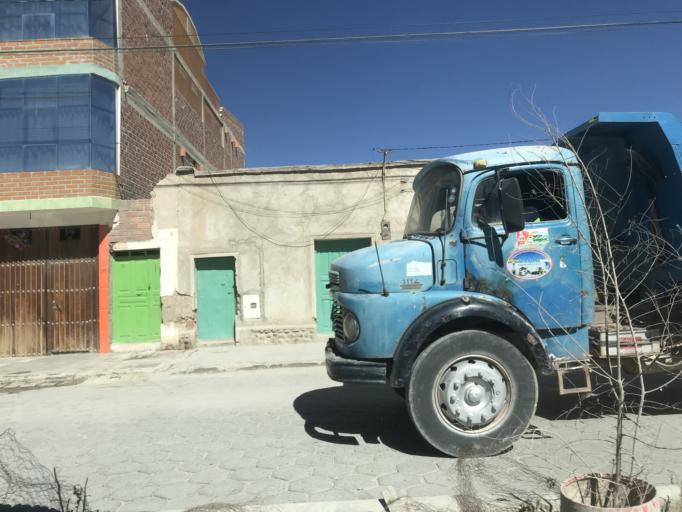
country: BO
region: Potosi
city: Uyuni
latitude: -20.4594
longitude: -66.8245
